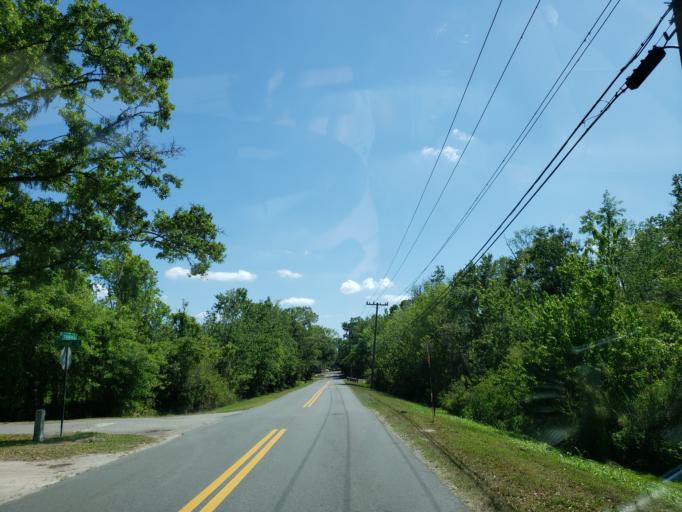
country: US
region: Florida
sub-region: Hillsborough County
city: Plant City
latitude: 28.0214
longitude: -82.1298
